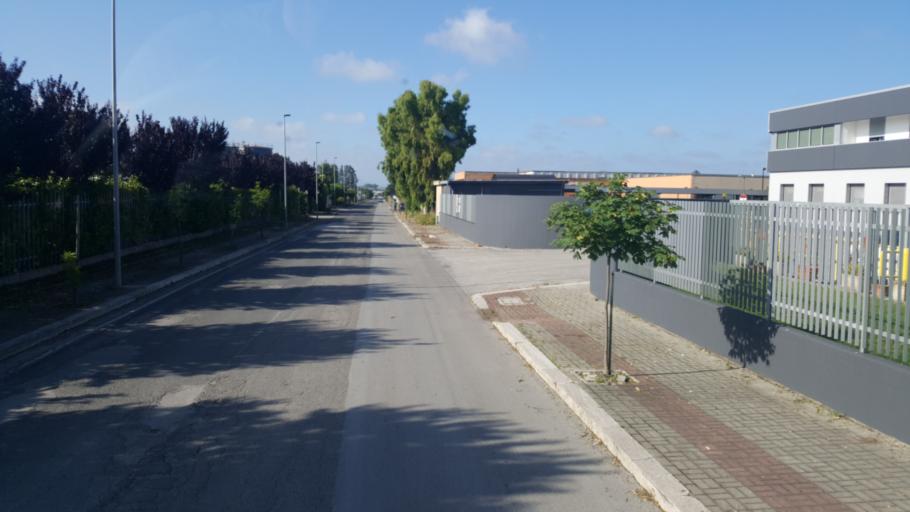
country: IT
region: Latium
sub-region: Provincia di Latina
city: Aprilia
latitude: 41.5780
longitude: 12.6468
